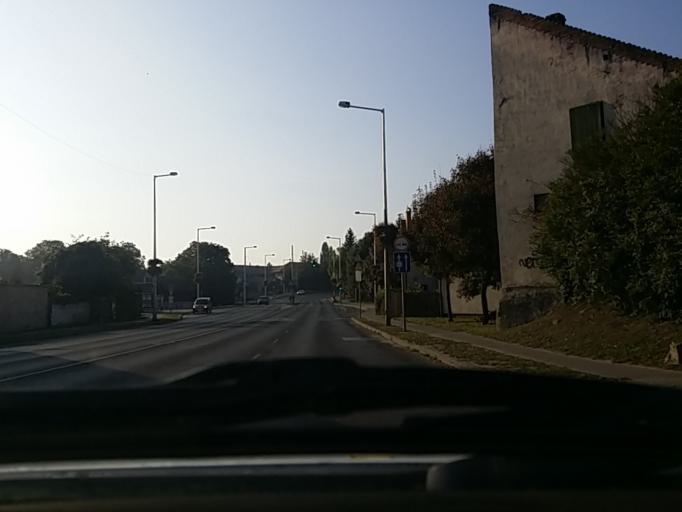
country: HU
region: Pest
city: Szentendre
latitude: 47.6686
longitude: 19.0714
